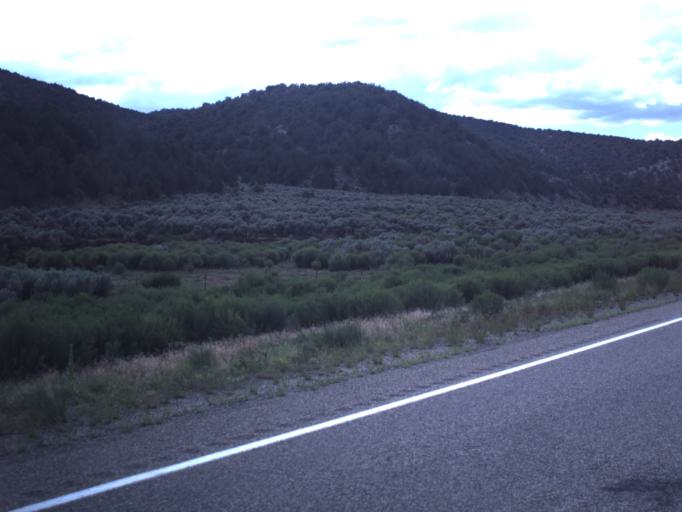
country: US
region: Utah
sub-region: Garfield County
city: Panguitch
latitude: 37.9854
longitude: -112.4896
